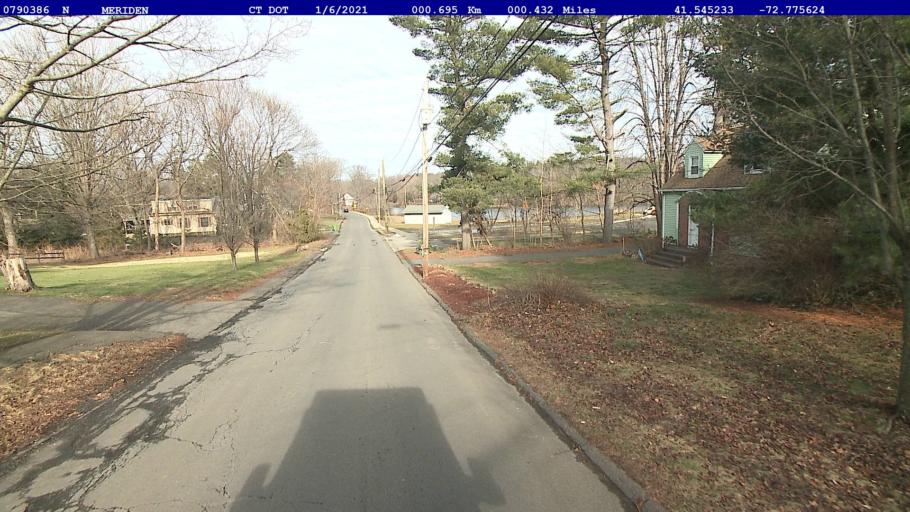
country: US
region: Connecticut
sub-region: New Haven County
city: Meriden
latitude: 41.5452
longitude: -72.7756
